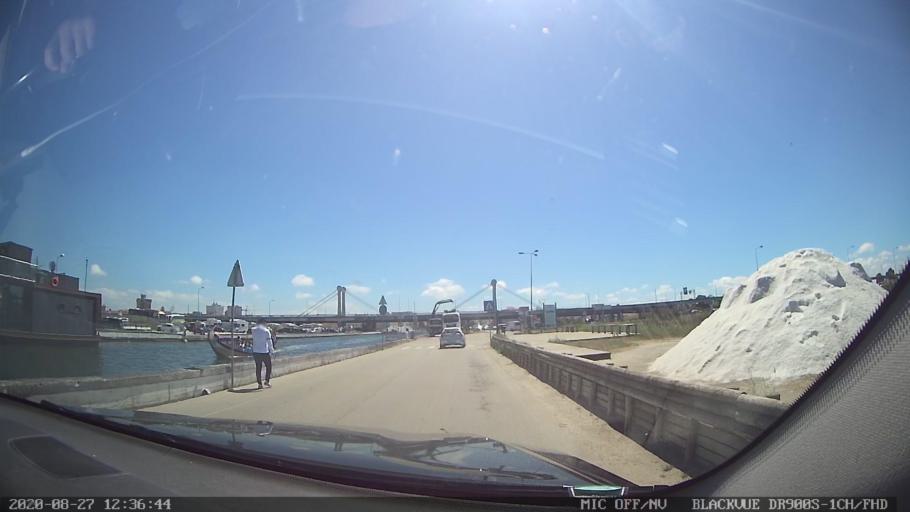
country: PT
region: Aveiro
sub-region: Aveiro
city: Aveiro
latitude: 40.6446
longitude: -8.6614
